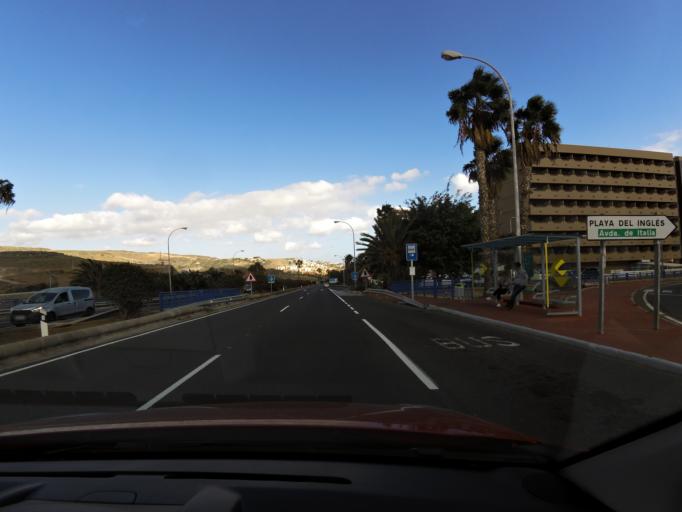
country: ES
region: Canary Islands
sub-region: Provincia de Las Palmas
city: Playa del Ingles
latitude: 27.7649
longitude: -15.5627
